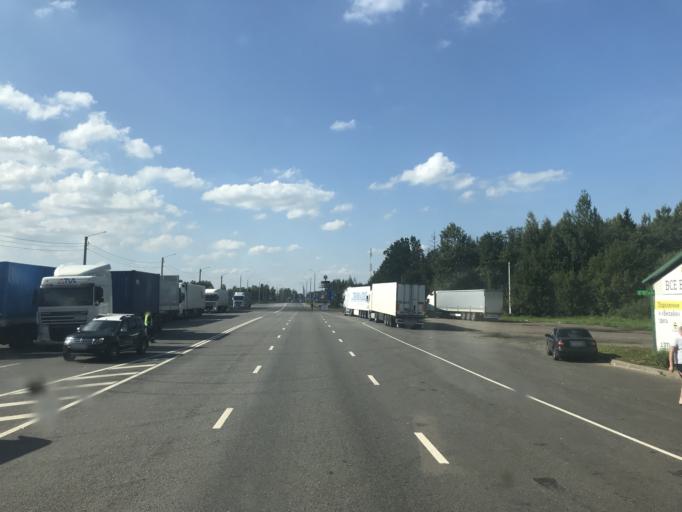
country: RU
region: Smolensk
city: Rudnya
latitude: 54.9882
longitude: 30.9552
